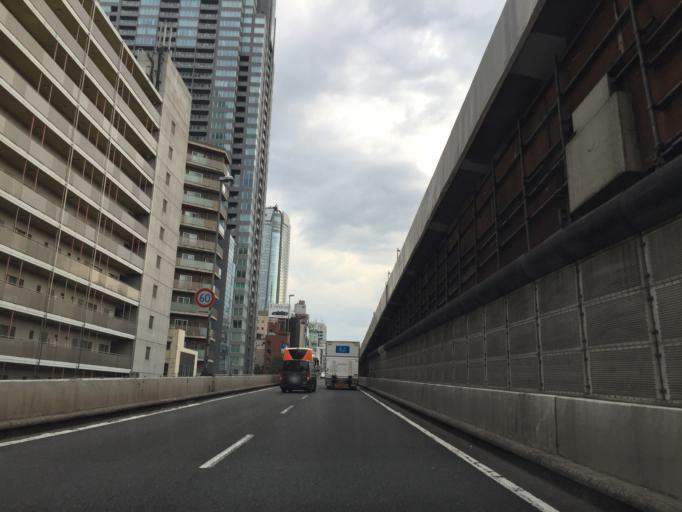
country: JP
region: Tokyo
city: Tokyo
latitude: 35.6652
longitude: 139.7362
